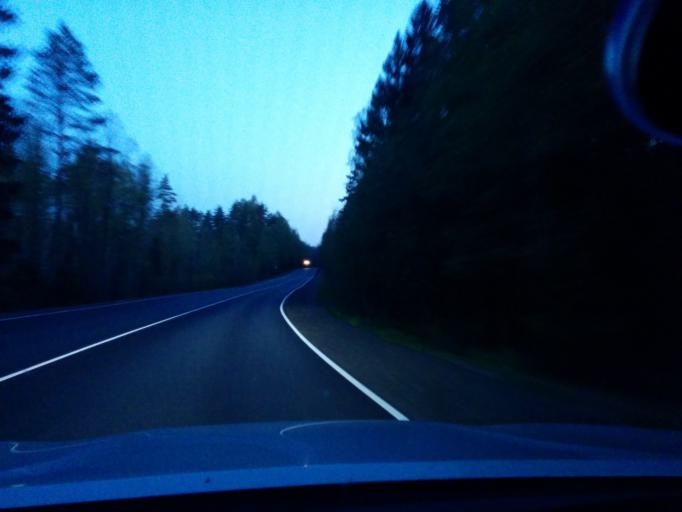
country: RU
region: Leningrad
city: Verkhniye Osel'ki
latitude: 60.1982
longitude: 30.4248
